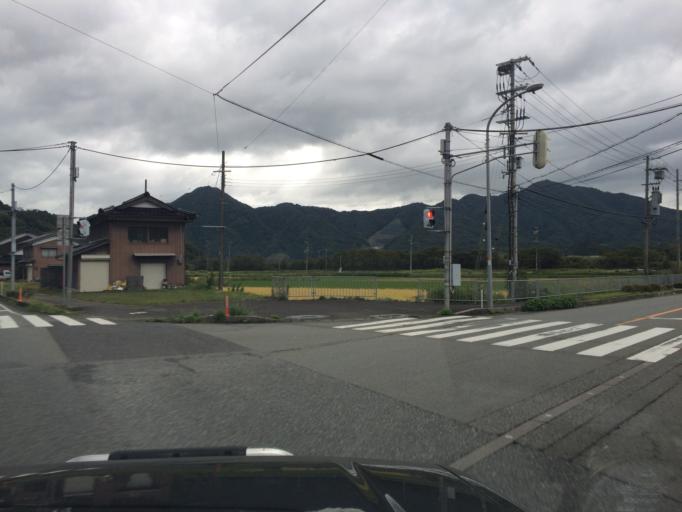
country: JP
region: Hyogo
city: Toyooka
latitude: 35.4246
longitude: 134.7899
